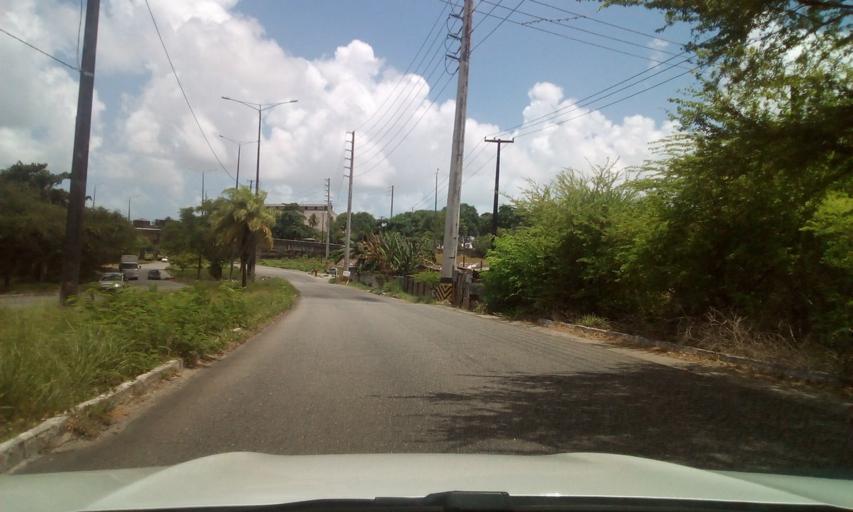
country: BR
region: Paraiba
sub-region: Joao Pessoa
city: Joao Pessoa
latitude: -7.1247
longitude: -34.8952
